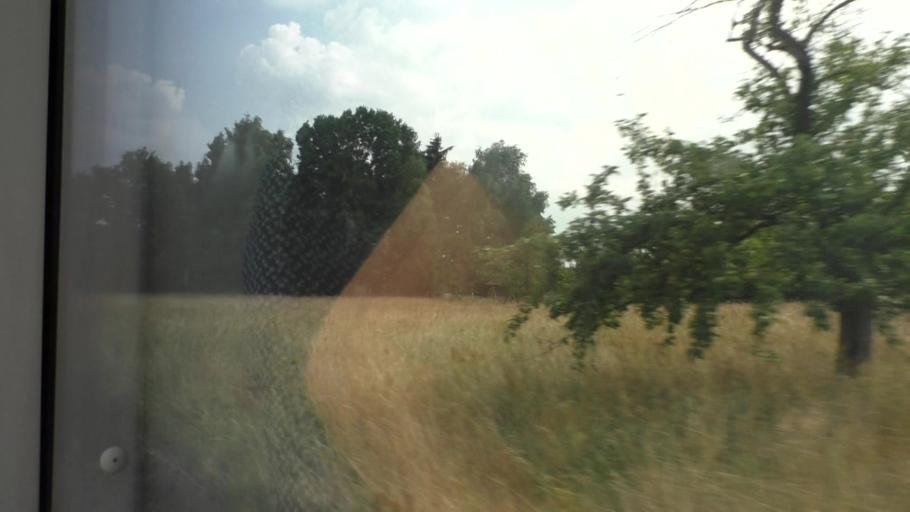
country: DE
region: Brandenburg
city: Beeskow
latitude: 52.1731
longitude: 14.2032
